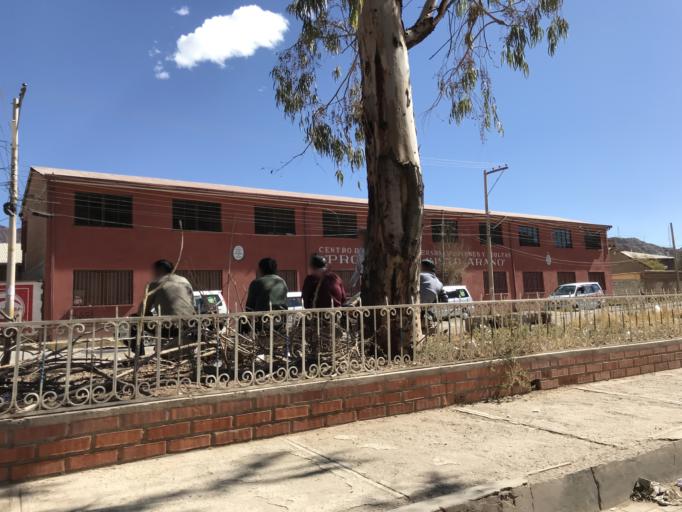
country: BO
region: Potosi
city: Tupiza
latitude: -21.4469
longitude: -65.7154
